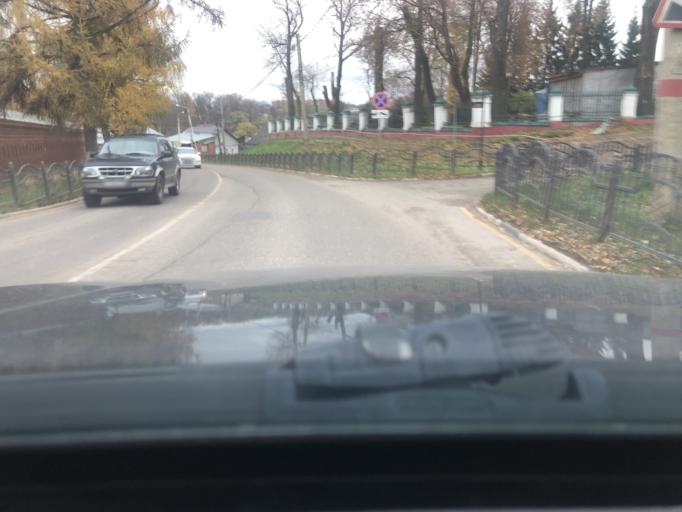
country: RU
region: Moskovskaya
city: Sergiyev Posad
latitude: 56.3078
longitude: 38.1257
